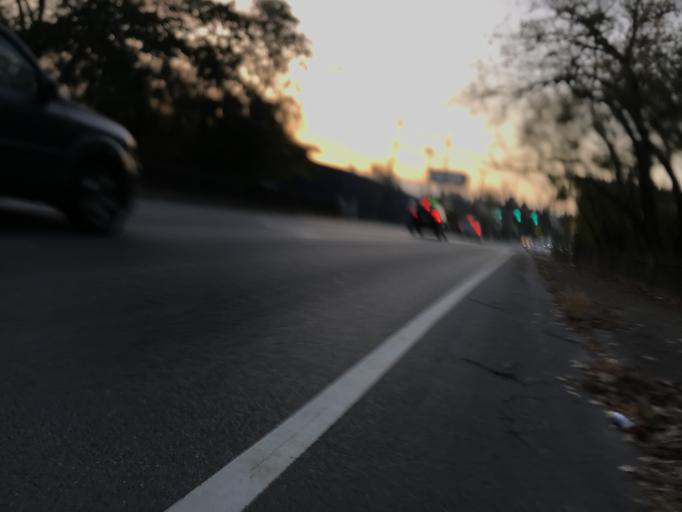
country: US
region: Indiana
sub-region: Clark County
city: Jeffersonville
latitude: 38.2561
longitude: -85.7231
